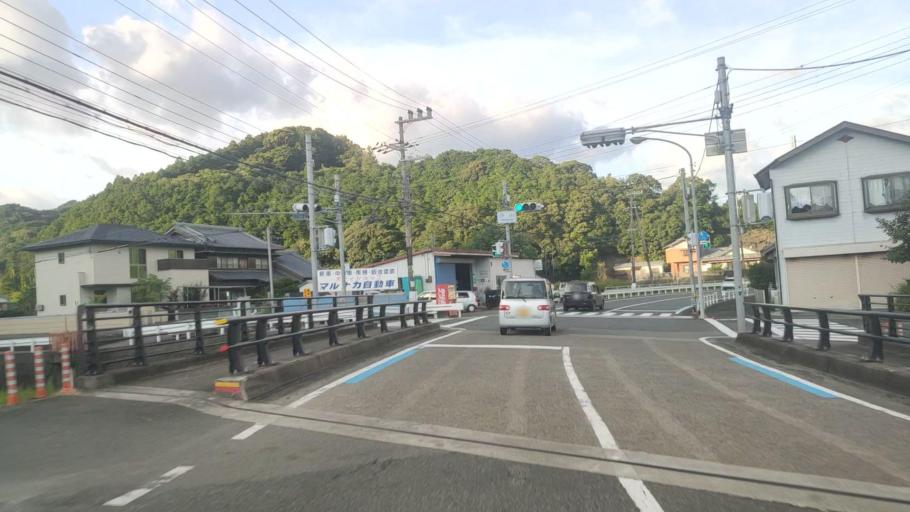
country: JP
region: Wakayama
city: Tanabe
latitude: 33.7184
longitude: 135.4723
